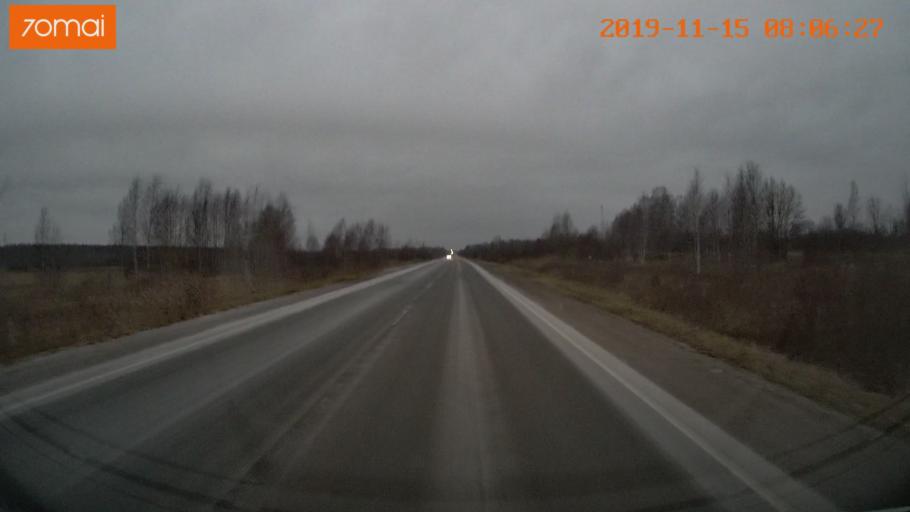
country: RU
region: Vologda
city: Cherepovets
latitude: 59.0217
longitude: 38.0403
